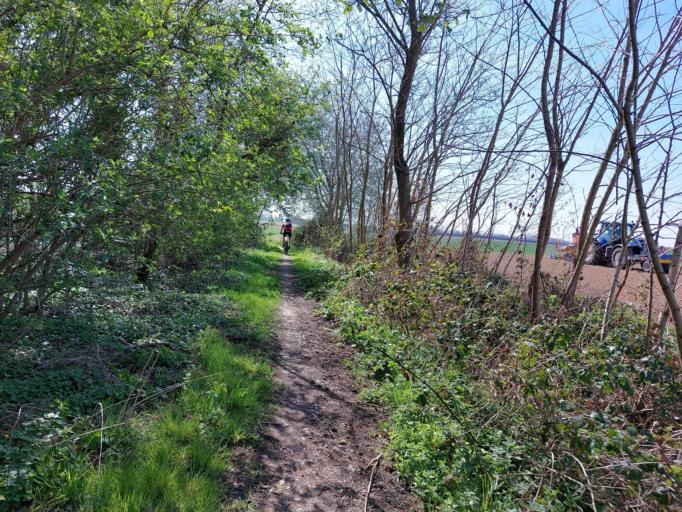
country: BE
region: Wallonia
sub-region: Province du Hainaut
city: Lens
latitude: 50.5944
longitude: 3.9064
